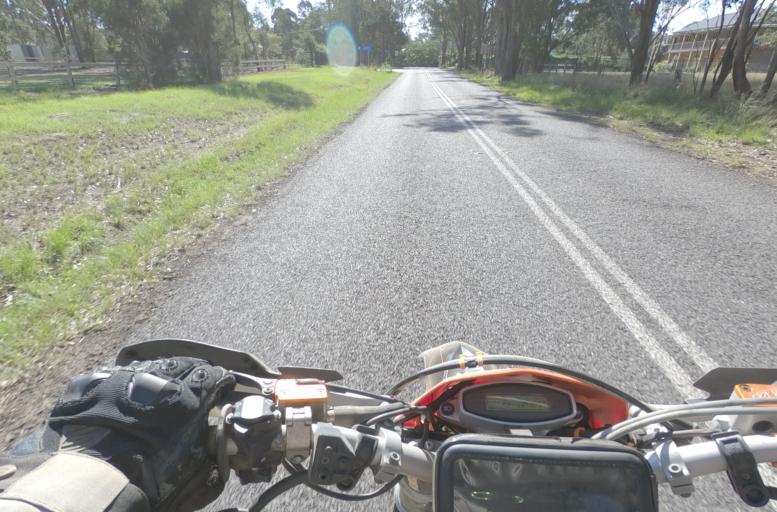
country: AU
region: New South Wales
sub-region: Hawkesbury
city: Scheyville
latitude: -33.5854
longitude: 150.8898
